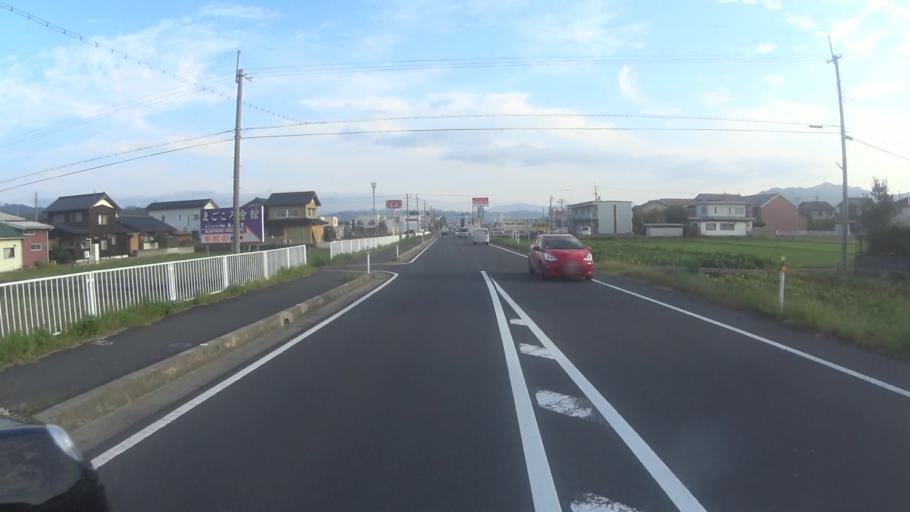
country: JP
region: Kyoto
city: Miyazu
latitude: 35.6193
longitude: 135.0752
